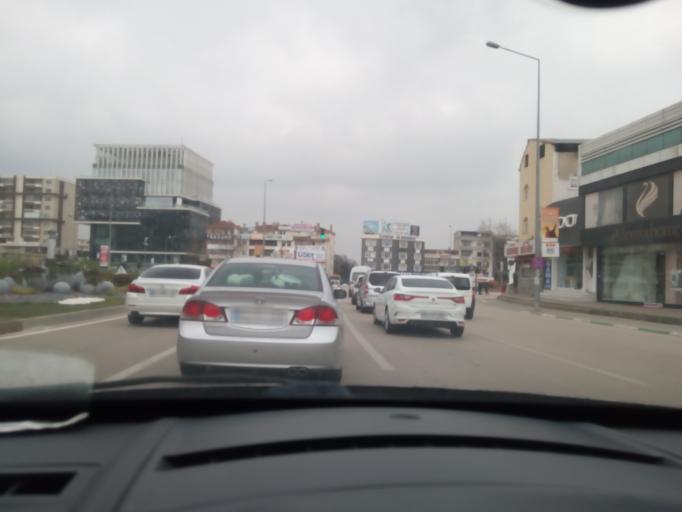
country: TR
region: Bursa
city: Yildirim
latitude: 40.2308
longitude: 28.9825
